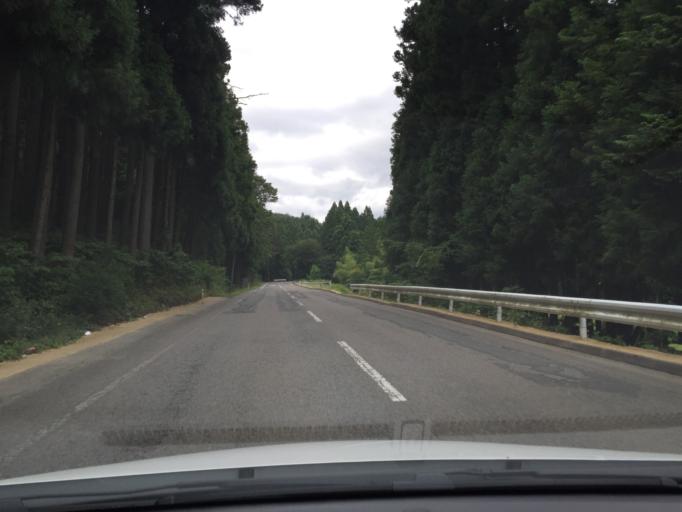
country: JP
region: Fukushima
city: Sukagawa
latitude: 37.1725
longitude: 140.1730
